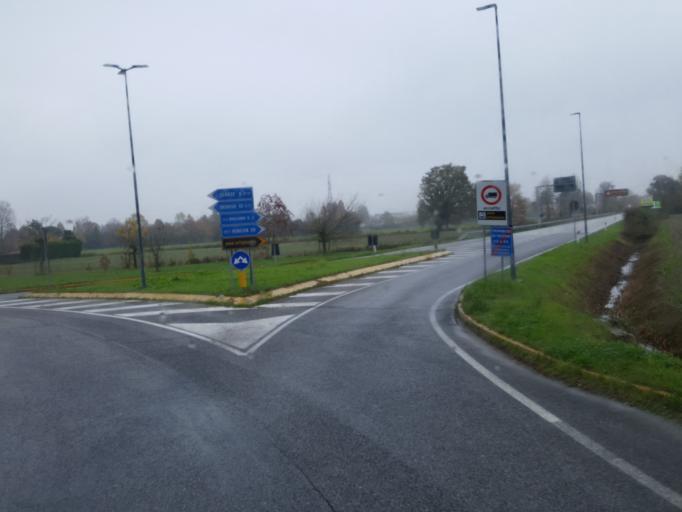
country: IT
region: Veneto
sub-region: Provincia di Treviso
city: Mogliano Veneto
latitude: 45.5611
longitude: 12.2146
